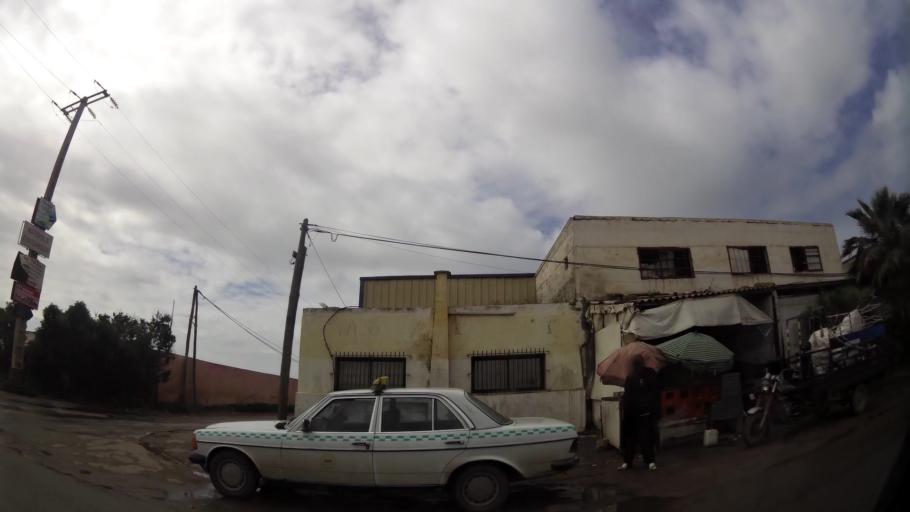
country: MA
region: Grand Casablanca
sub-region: Mediouna
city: Tit Mellil
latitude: 33.6439
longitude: -7.4761
